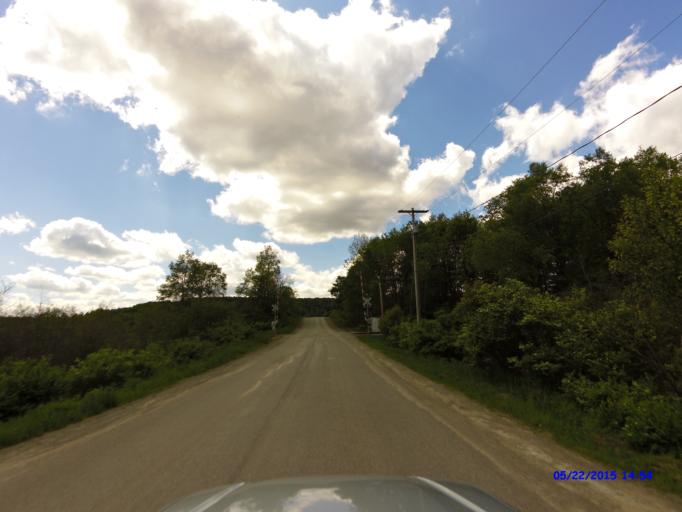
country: US
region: New York
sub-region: Cattaraugus County
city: Franklinville
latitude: 42.3779
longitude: -78.5969
